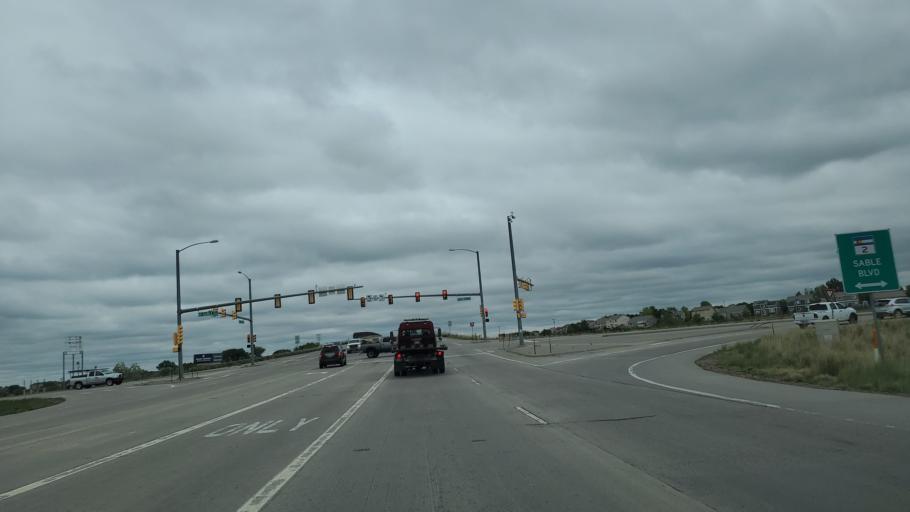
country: US
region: Colorado
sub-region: Adams County
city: Brighton
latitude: 39.9144
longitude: -104.8199
